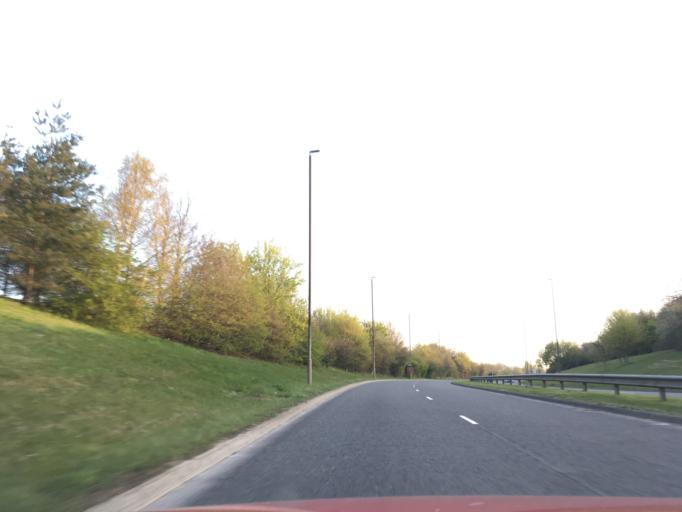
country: GB
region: England
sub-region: Gloucestershire
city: Churchdown
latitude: 51.8517
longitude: -2.1718
